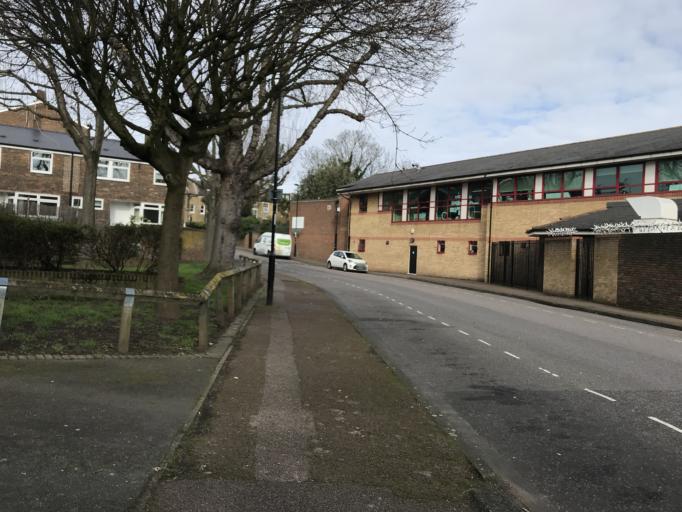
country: GB
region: England
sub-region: Greater London
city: Catford
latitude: 51.4738
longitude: -0.0280
